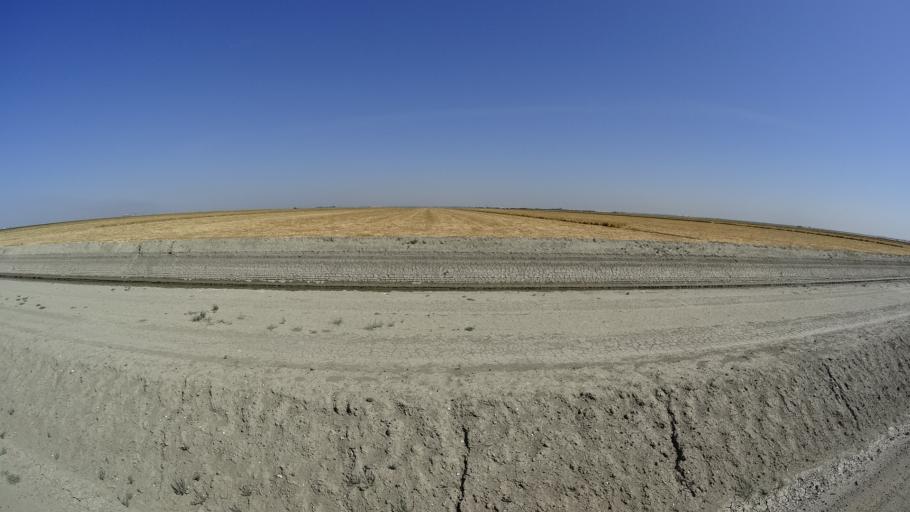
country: US
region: California
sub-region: Tulare County
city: Alpaugh
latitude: 35.9780
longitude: -119.5575
